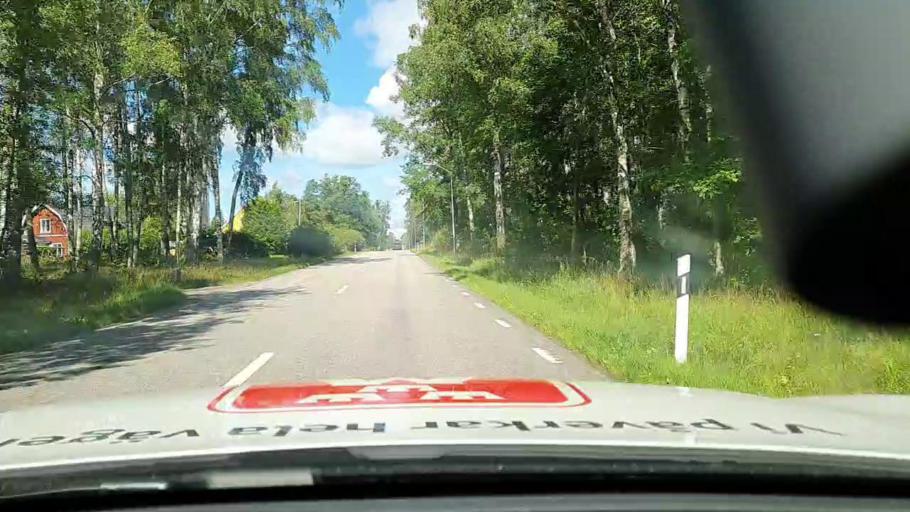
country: SE
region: Vaestra Goetaland
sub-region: Skovde Kommun
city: Stopen
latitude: 58.5599
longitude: 14.0073
